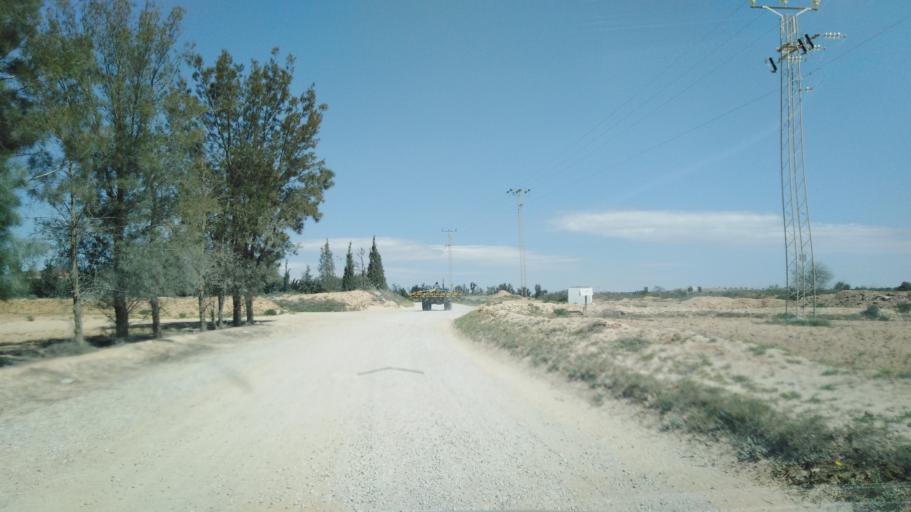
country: TN
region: Safaqis
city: Sfax
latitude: 34.7584
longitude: 10.5289
